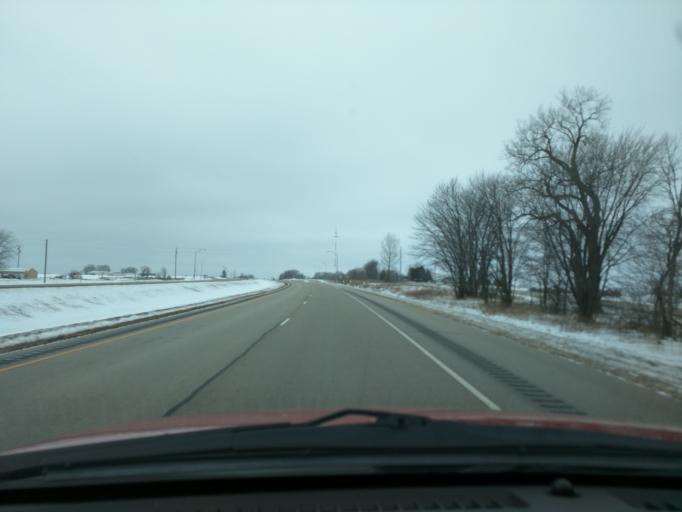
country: US
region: Wisconsin
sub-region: Trempealeau County
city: Trempealeau
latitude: 43.9117
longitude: -91.5471
